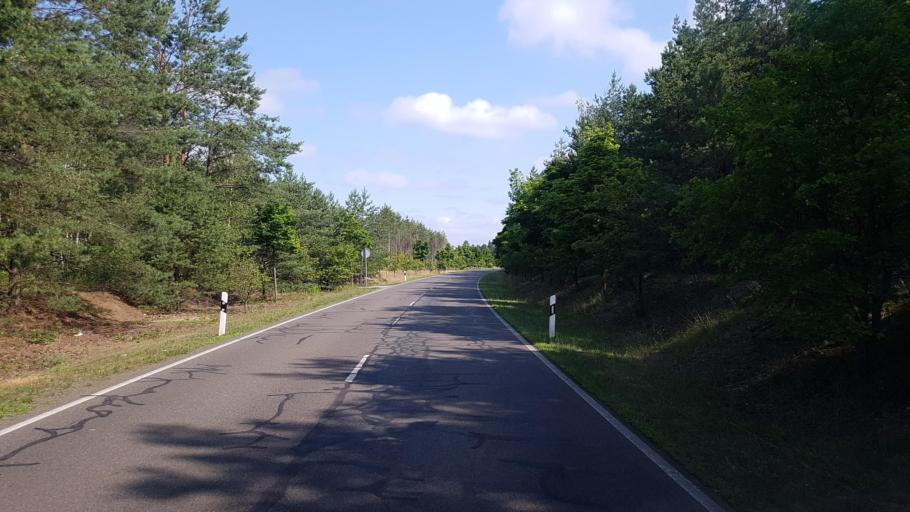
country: DE
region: Brandenburg
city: Grossraschen
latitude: 51.5894
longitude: 14.0283
